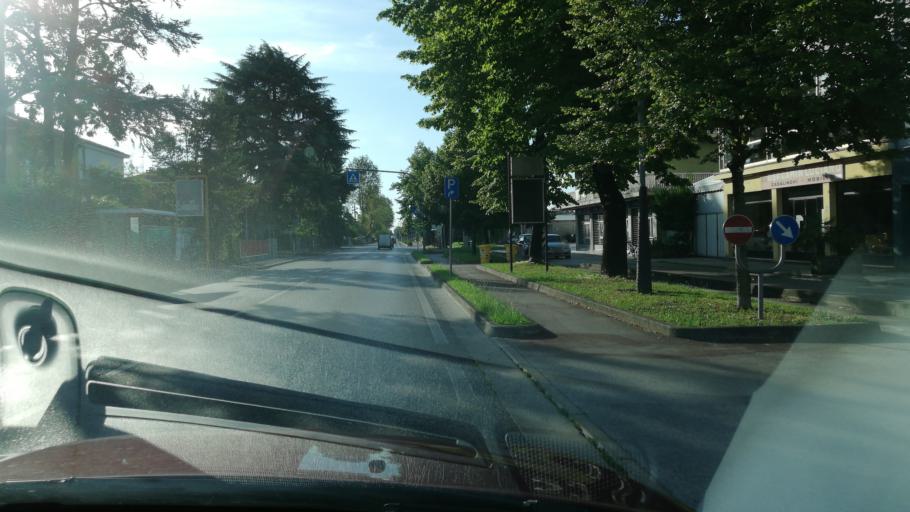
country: IT
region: Veneto
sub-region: Provincia di Venezia
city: Santo Stino di Livenza
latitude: 45.7289
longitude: 12.6845
